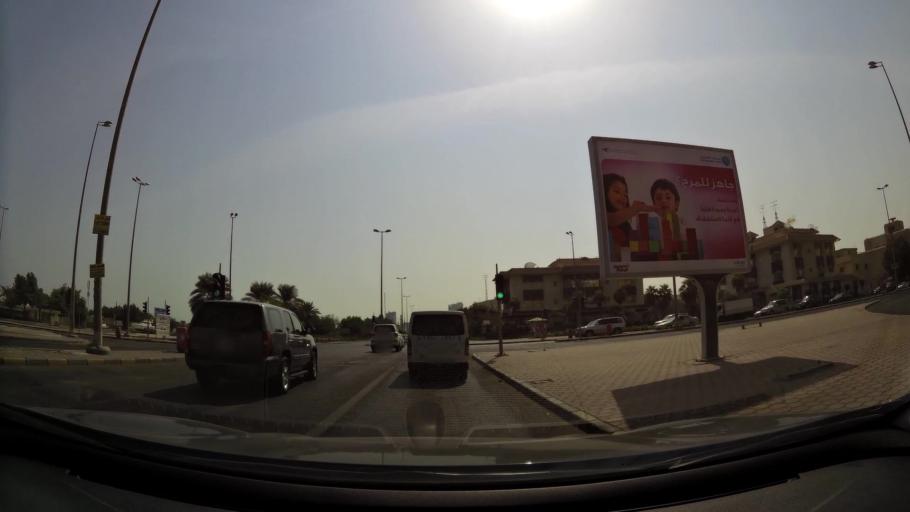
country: KW
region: Al Ahmadi
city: Al Manqaf
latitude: 29.0924
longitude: 48.1375
